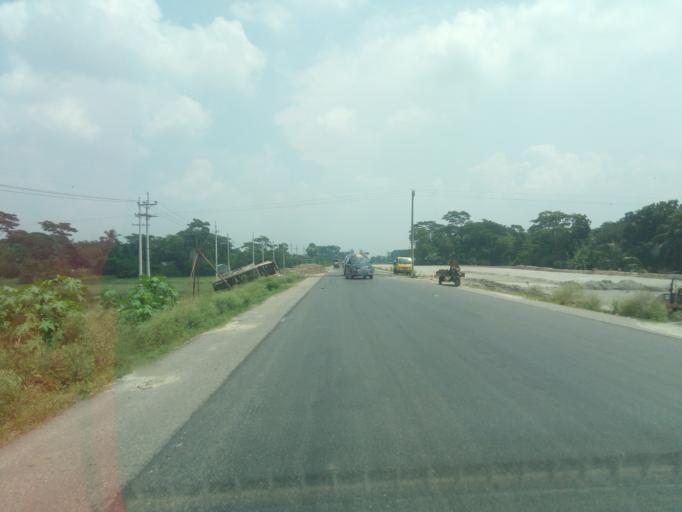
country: BD
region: Dhaka
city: Char Bhadrasan
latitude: 23.3755
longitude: 90.0225
